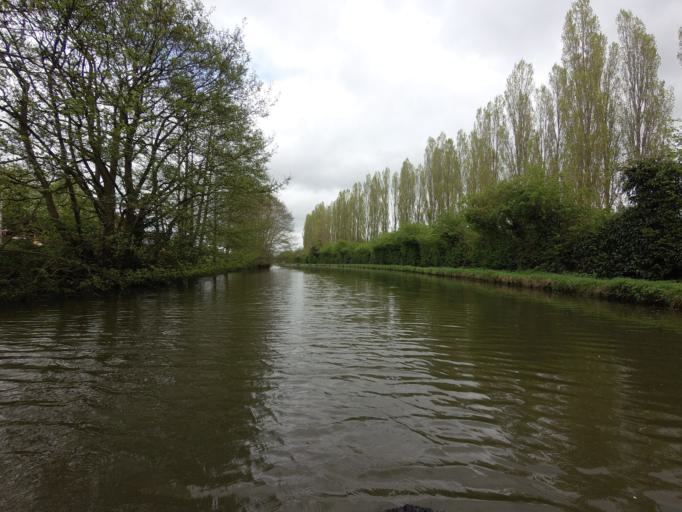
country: GB
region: England
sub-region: Milton Keynes
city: Water Eaton
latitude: 51.9848
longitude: -0.7178
